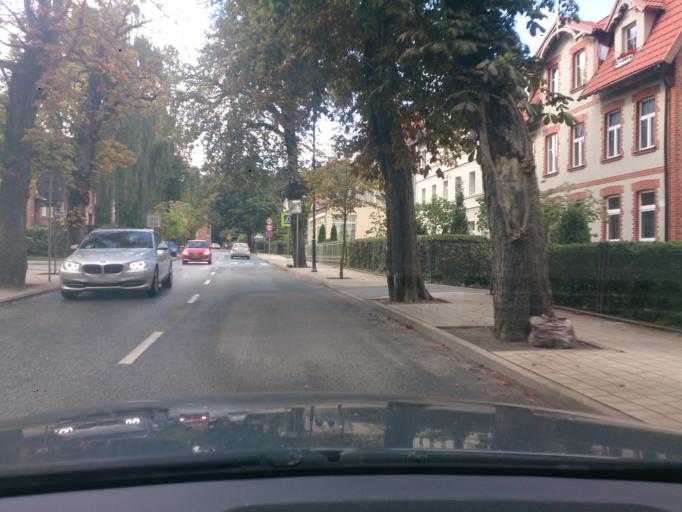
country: PL
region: Pomeranian Voivodeship
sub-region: Sopot
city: Sopot
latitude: 54.4508
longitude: 18.5518
